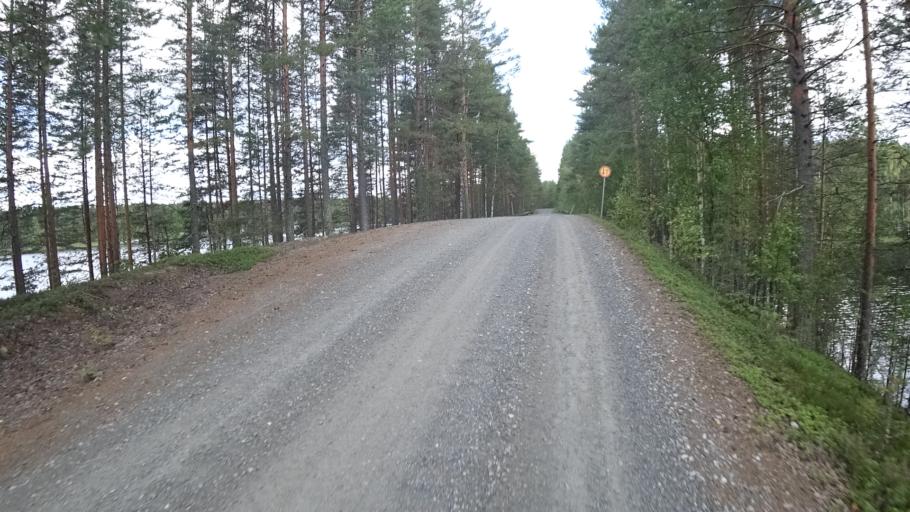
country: FI
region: North Karelia
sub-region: Joensuu
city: Ilomantsi
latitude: 62.6153
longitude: 31.1963
